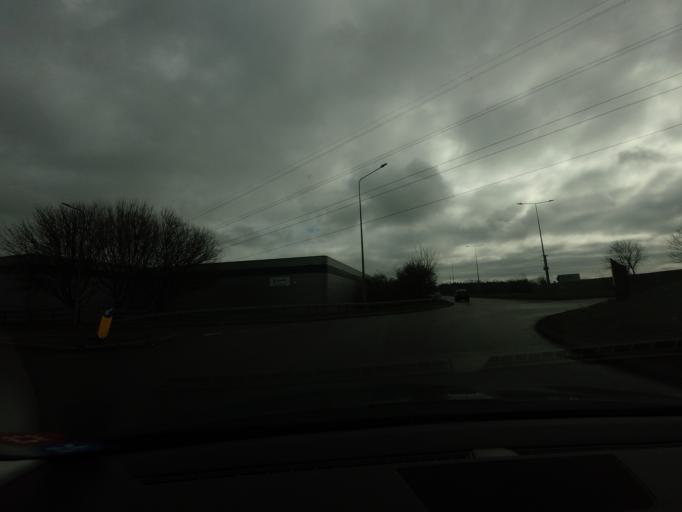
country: GB
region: England
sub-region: Kent
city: Eynsford
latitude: 51.3862
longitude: 0.1973
